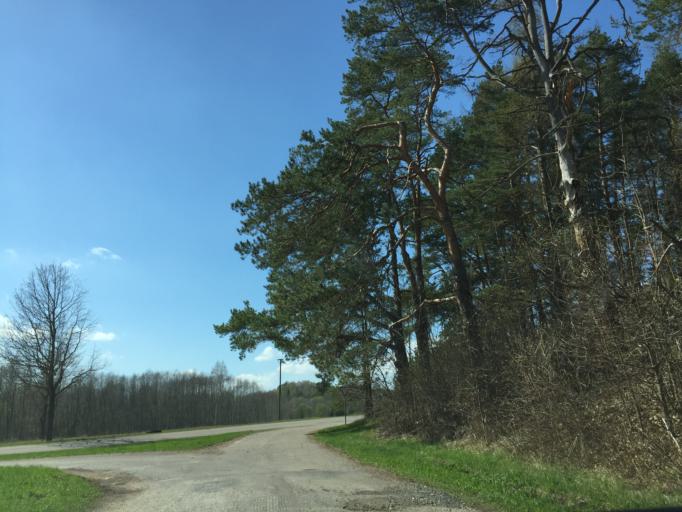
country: EE
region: Tartu
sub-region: Elva linn
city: Elva
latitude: 58.1533
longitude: 26.2272
